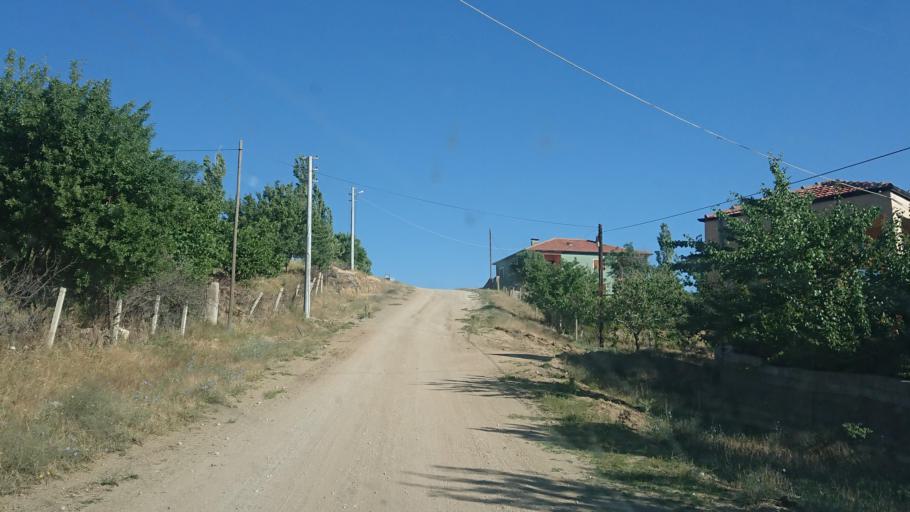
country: TR
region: Aksaray
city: Agacoren
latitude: 38.8731
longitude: 33.9433
